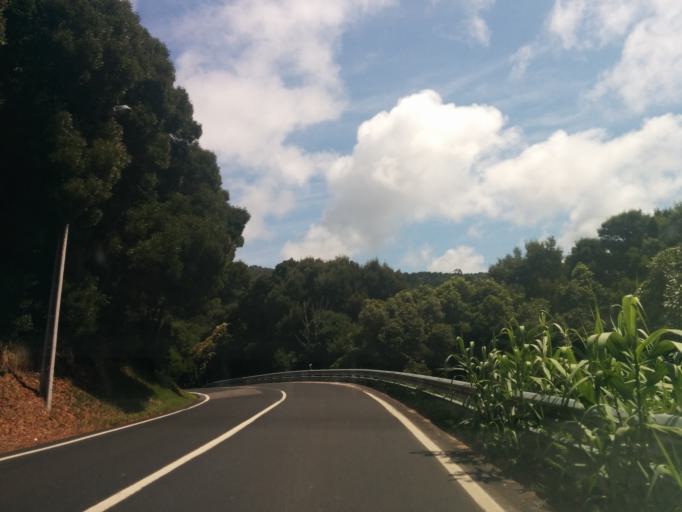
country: PT
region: Lisbon
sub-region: Sintra
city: Colares
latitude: 38.7731
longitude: -9.4739
